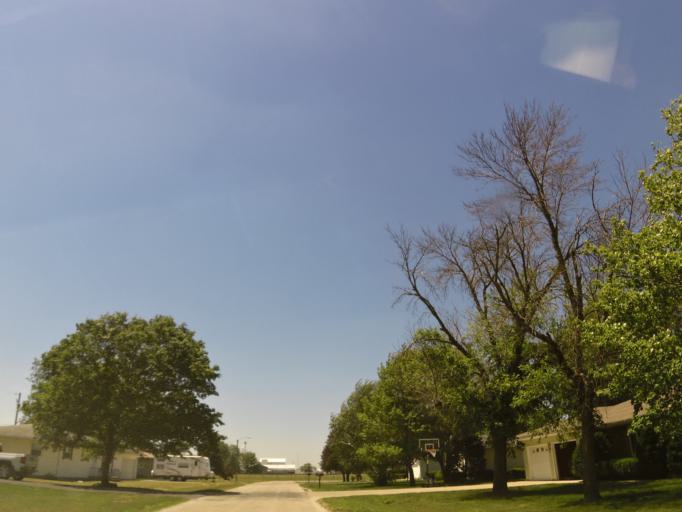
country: US
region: Illinois
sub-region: Livingston County
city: Chatsworth
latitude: 40.7523
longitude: -88.1849
